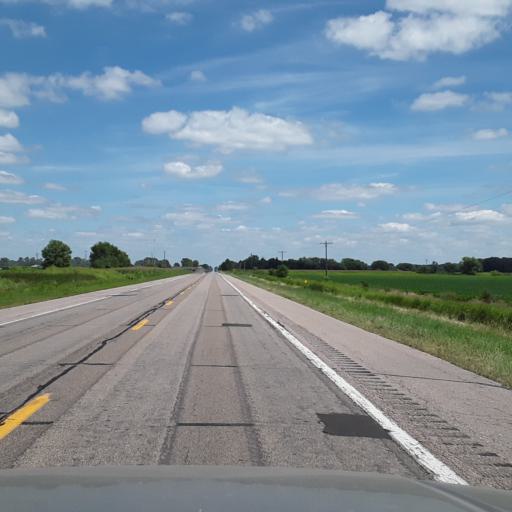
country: US
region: Nebraska
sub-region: Polk County
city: Osceola
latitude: 41.3579
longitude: -97.5647
